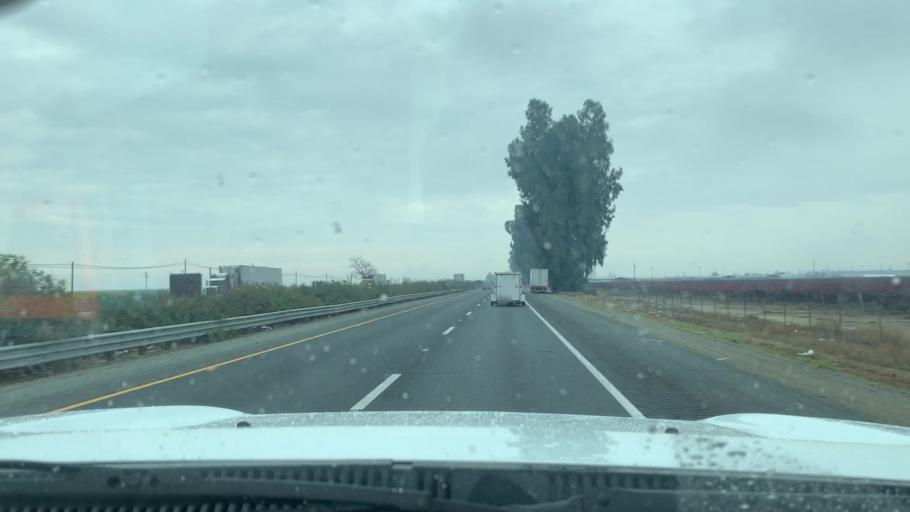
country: US
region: California
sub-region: Kern County
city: Delano
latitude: 35.8089
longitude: -119.2566
